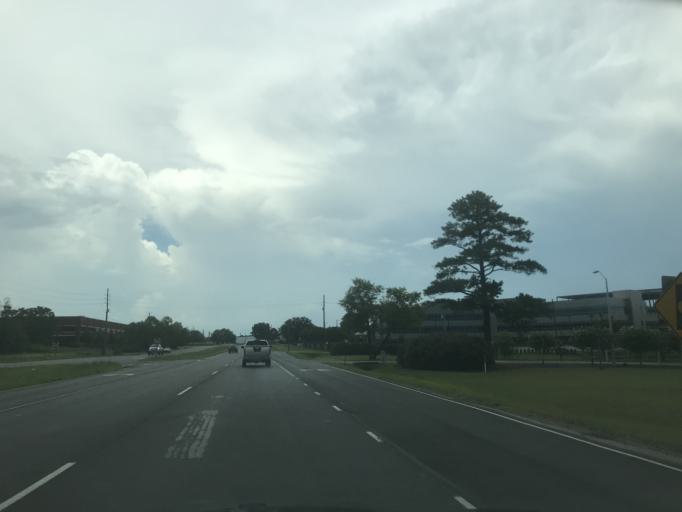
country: US
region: North Carolina
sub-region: Johnston County
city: Clayton
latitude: 35.6165
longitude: -78.4190
